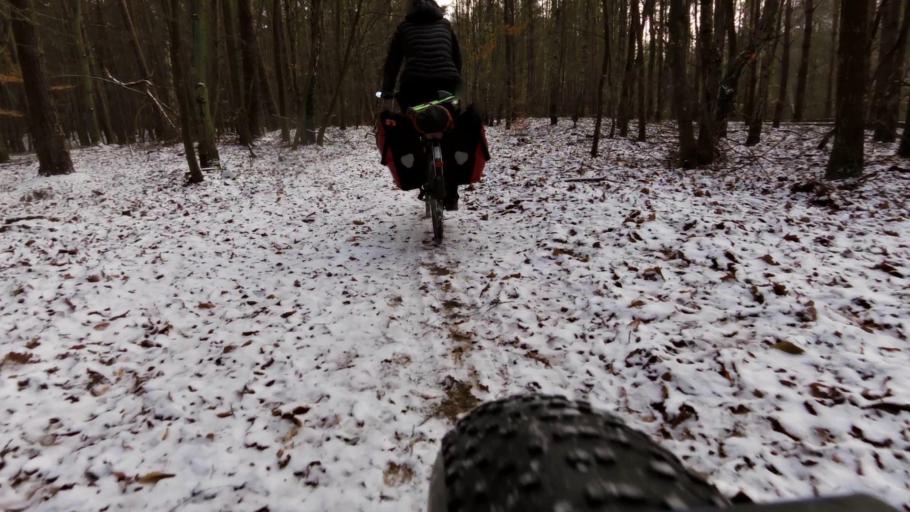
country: PL
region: West Pomeranian Voivodeship
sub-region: Powiat walecki
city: Tuczno
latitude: 53.2974
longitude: 16.2902
